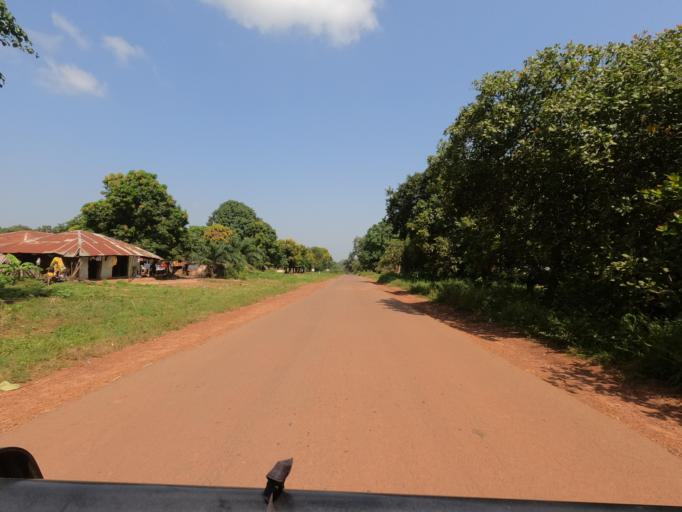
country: GW
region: Oio
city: Bissora
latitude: 12.3261
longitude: -15.7593
